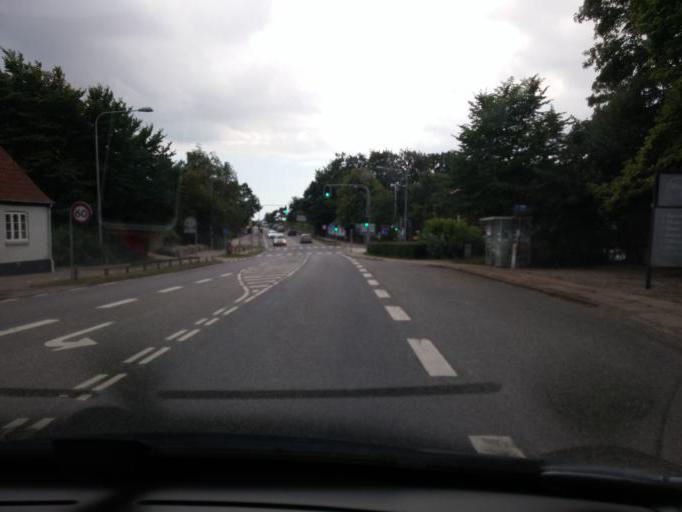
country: DK
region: South Denmark
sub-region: Svendborg Kommune
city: Vindeby
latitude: 55.0222
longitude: 10.6075
